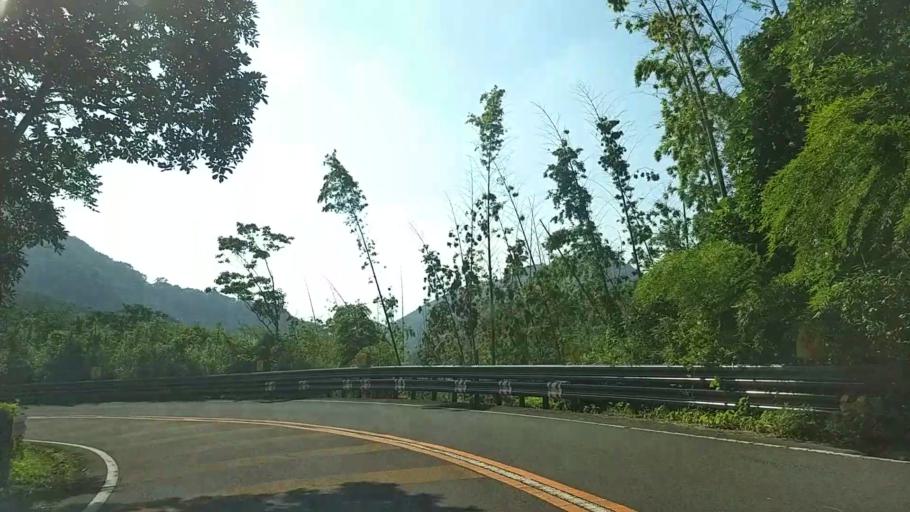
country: JP
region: Shizuoka
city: Shimoda
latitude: 34.7175
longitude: 138.7608
